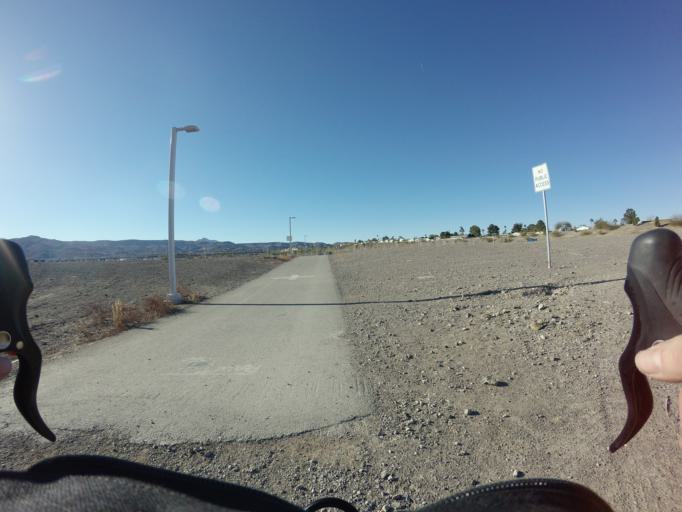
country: US
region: Nevada
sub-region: Clark County
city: Whitney
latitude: 36.0410
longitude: -115.0536
